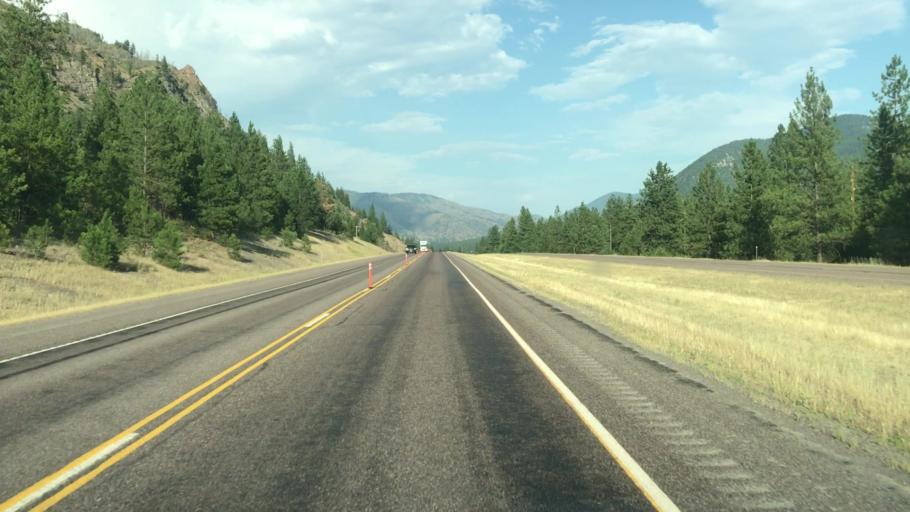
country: US
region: Montana
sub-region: Mineral County
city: Superior
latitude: 47.0121
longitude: -114.7129
